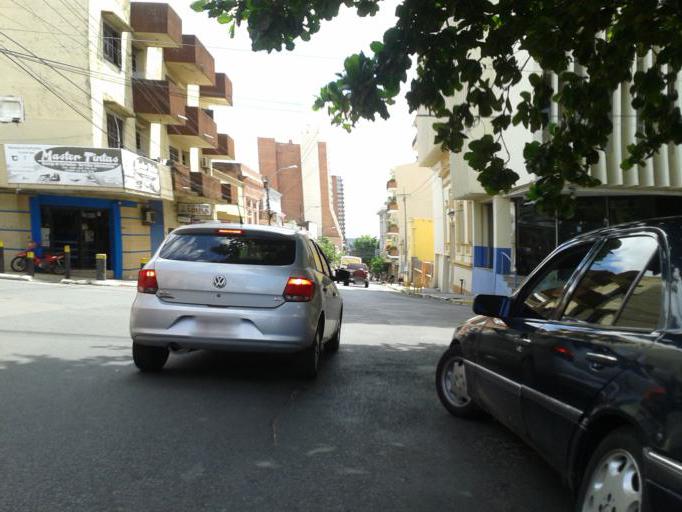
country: PY
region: Asuncion
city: Asuncion
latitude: -25.2883
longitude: -57.6335
